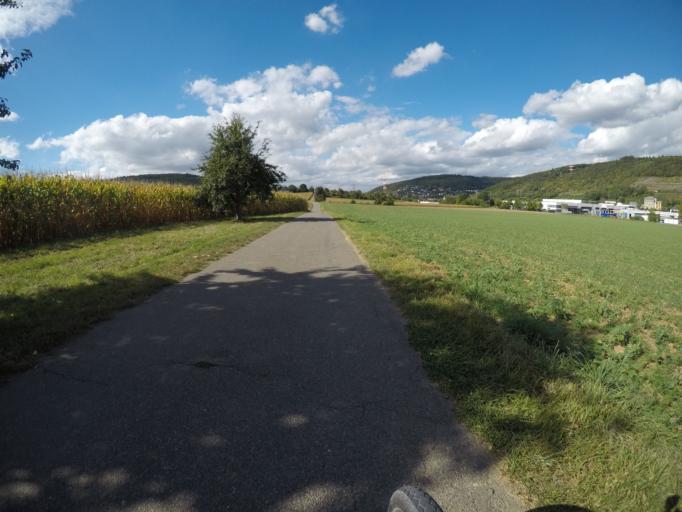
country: DE
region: Baden-Wuerttemberg
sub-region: Karlsruhe Region
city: Neckarzimmern
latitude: 49.3082
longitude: 9.1380
